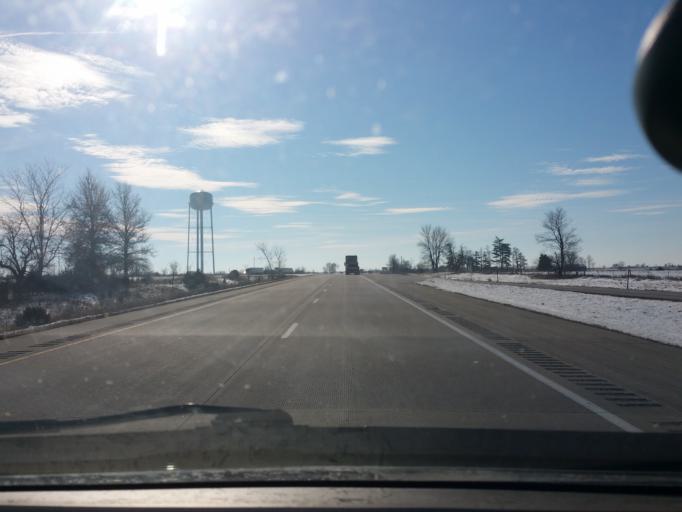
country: US
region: Iowa
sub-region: Clarke County
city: Osceola
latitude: 40.9906
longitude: -93.7986
